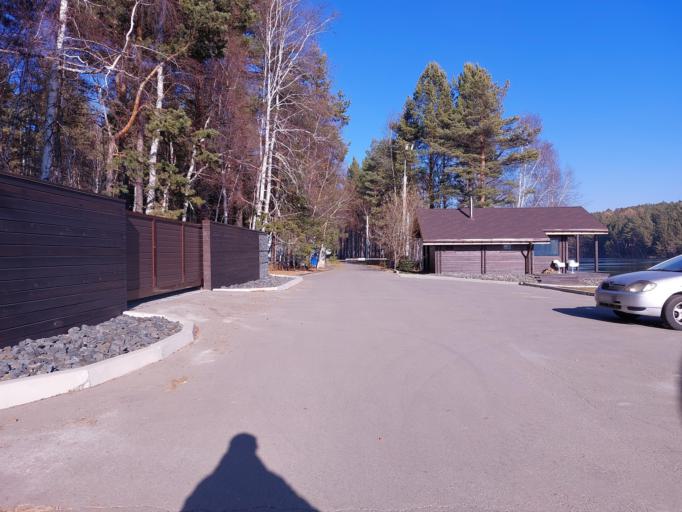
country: RU
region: Irkutsk
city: Pivovarikha
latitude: 52.1876
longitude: 104.4661
